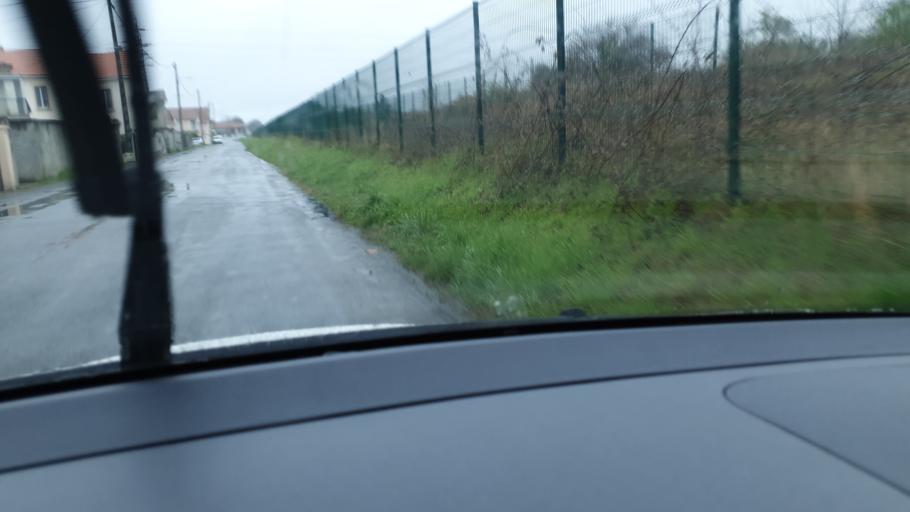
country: FR
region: Midi-Pyrenees
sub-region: Departement des Hautes-Pyrenees
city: Tarbes
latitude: 43.2499
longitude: 0.0535
